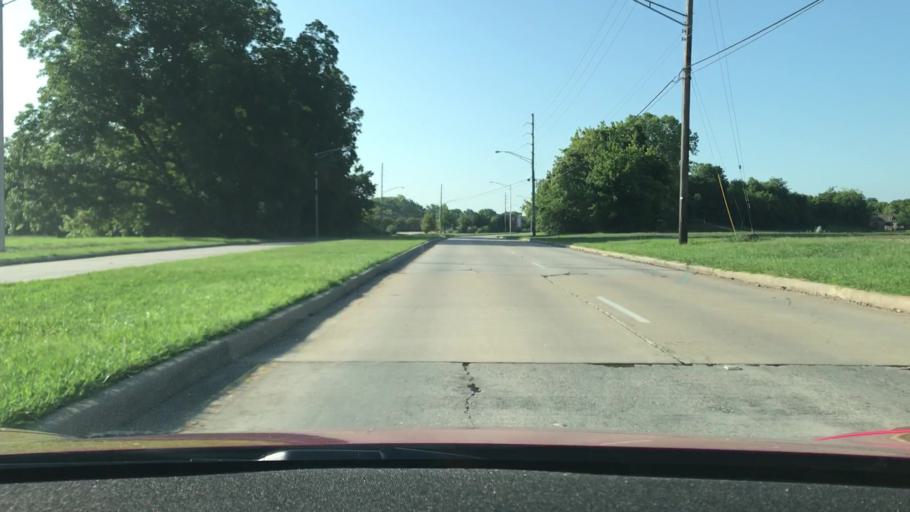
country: US
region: Louisiana
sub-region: Bossier Parish
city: Bossier City
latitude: 32.4356
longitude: -93.7281
